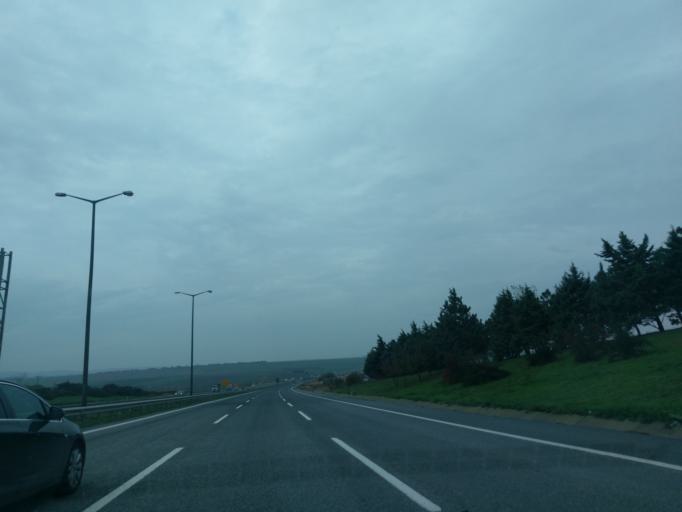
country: TR
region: Istanbul
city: Silivri
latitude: 41.1206
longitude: 28.1776
